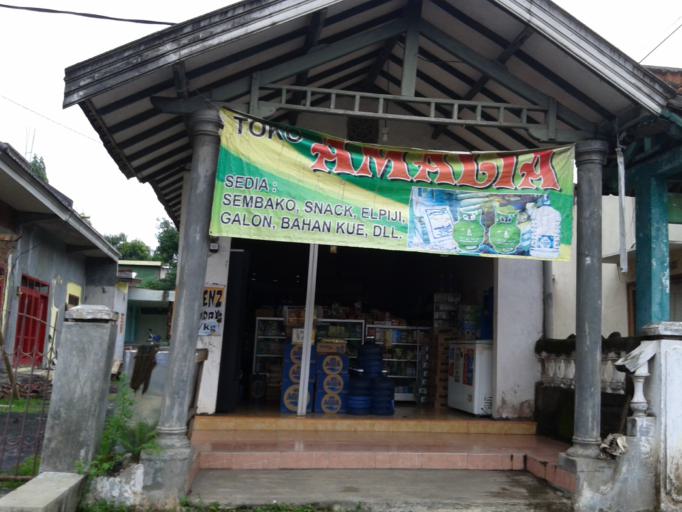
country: ID
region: East Java
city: Singosari
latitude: -7.8864
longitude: 112.6487
